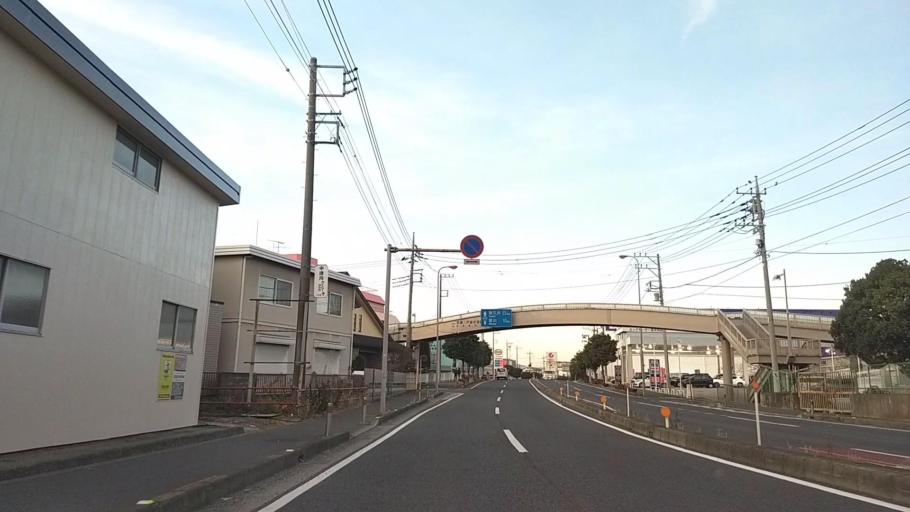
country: JP
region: Kanagawa
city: Atsugi
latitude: 35.4526
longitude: 139.3534
